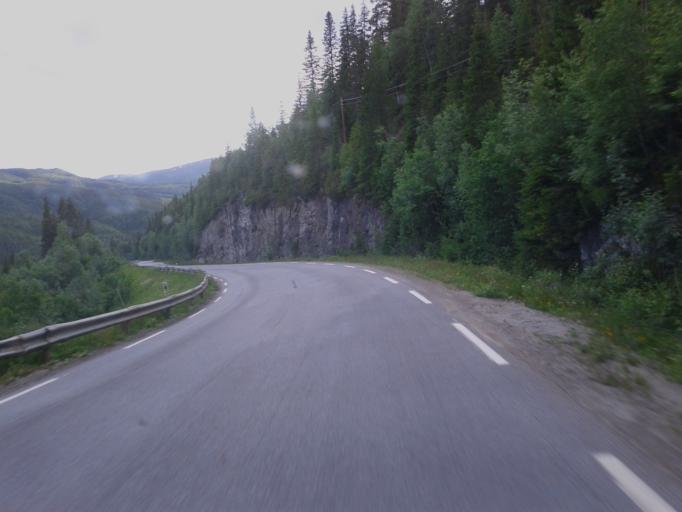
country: NO
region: Nordland
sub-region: Grane
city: Trofors
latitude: 65.5232
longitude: 13.6452
